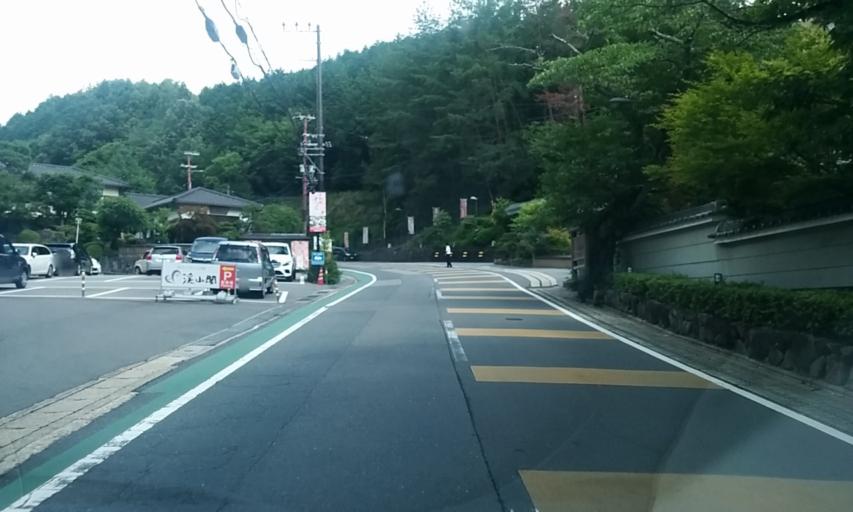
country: JP
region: Kyoto
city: Kameoka
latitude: 35.0178
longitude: 135.5196
